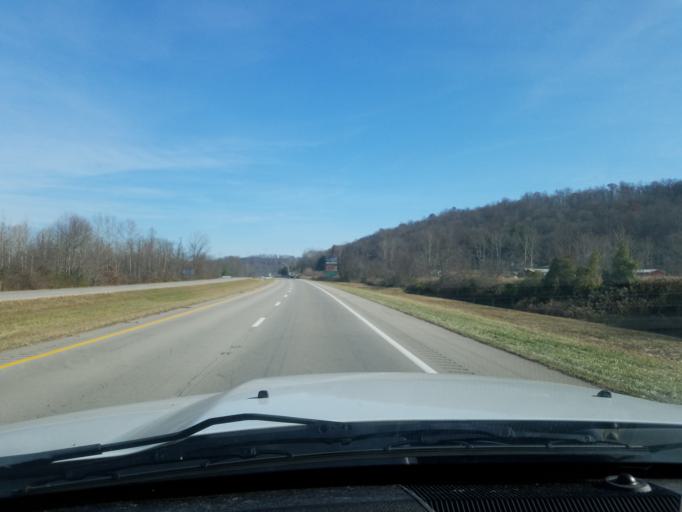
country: US
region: Ohio
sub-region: Pike County
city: Piketon
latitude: 39.0436
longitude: -83.1493
